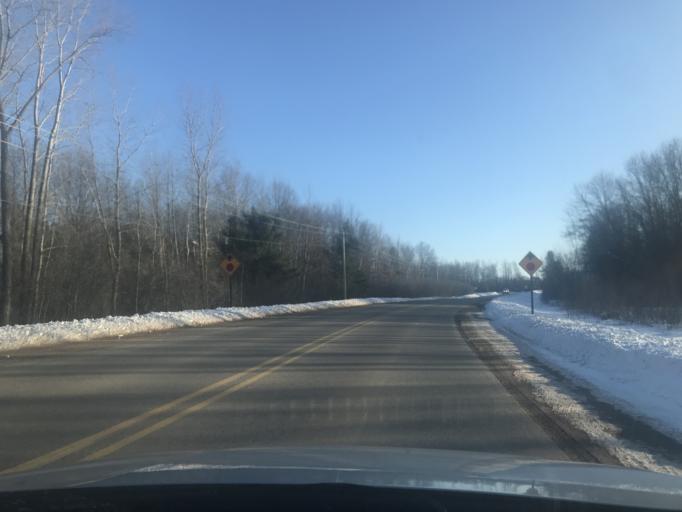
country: US
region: Wisconsin
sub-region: Marinette County
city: Marinette
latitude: 45.1180
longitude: -87.6467
